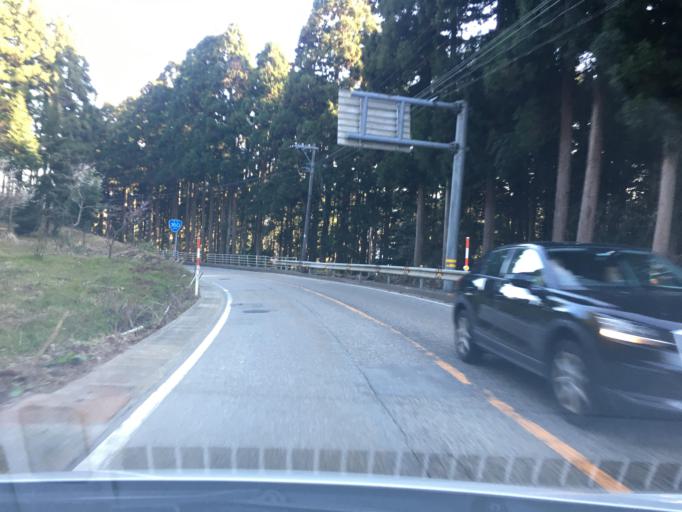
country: JP
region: Ishikawa
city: Nanao
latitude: 36.9814
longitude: 137.0496
